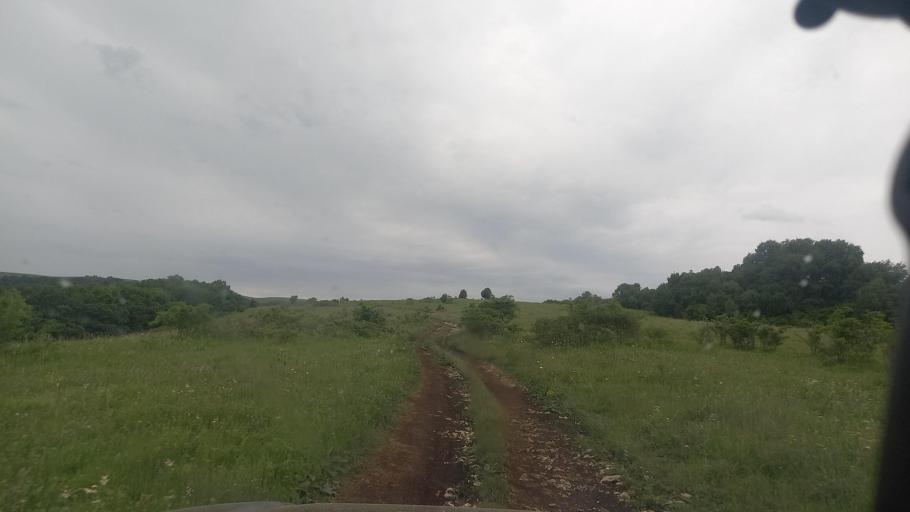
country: RU
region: Karachayevo-Cherkesiya
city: Pregradnaya
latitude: 44.0195
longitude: 41.2845
